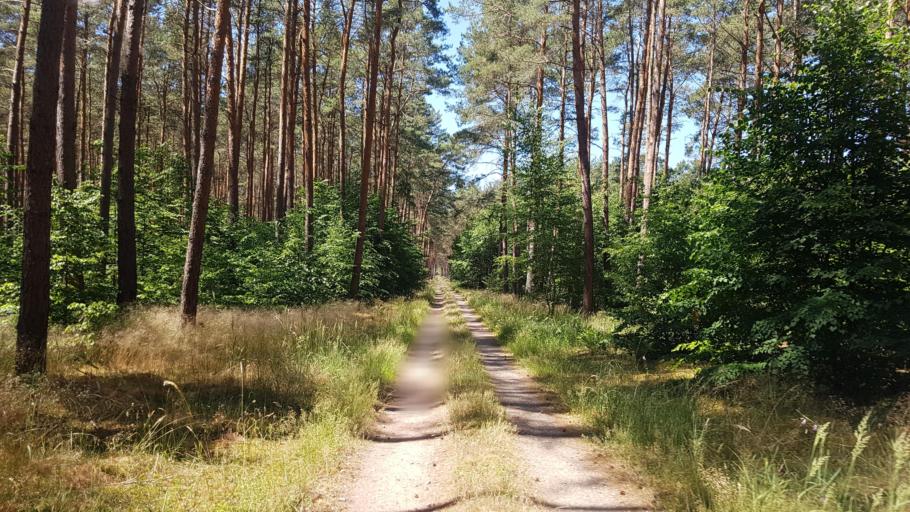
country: DE
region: Brandenburg
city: Treuenbrietzen
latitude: 52.0439
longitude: 12.8516
